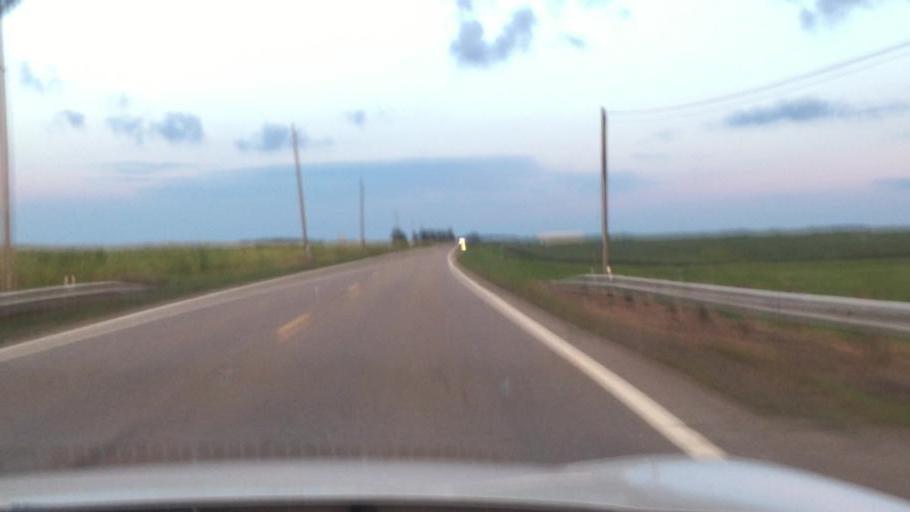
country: US
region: Ohio
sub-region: Madison County
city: Choctaw Lake
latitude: 40.0087
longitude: -83.4486
